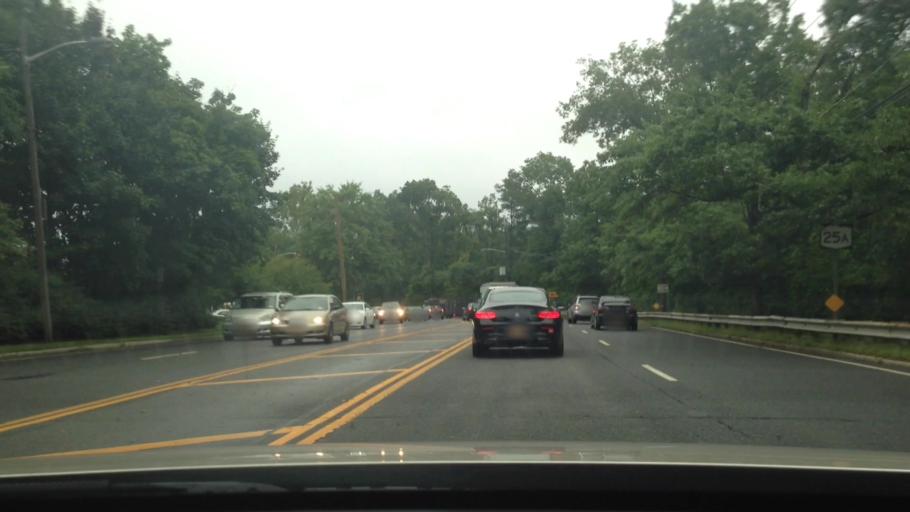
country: US
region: New York
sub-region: Nassau County
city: Thomaston
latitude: 40.7866
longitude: -73.7053
